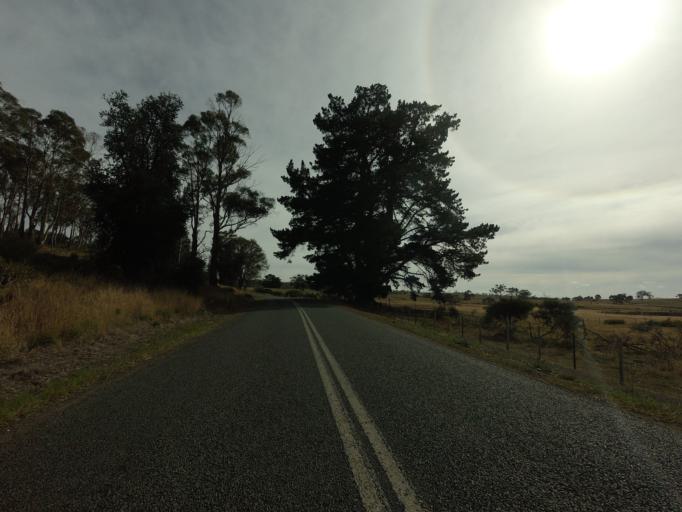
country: AU
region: Tasmania
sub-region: Brighton
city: Bridgewater
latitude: -42.3457
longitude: 147.4046
